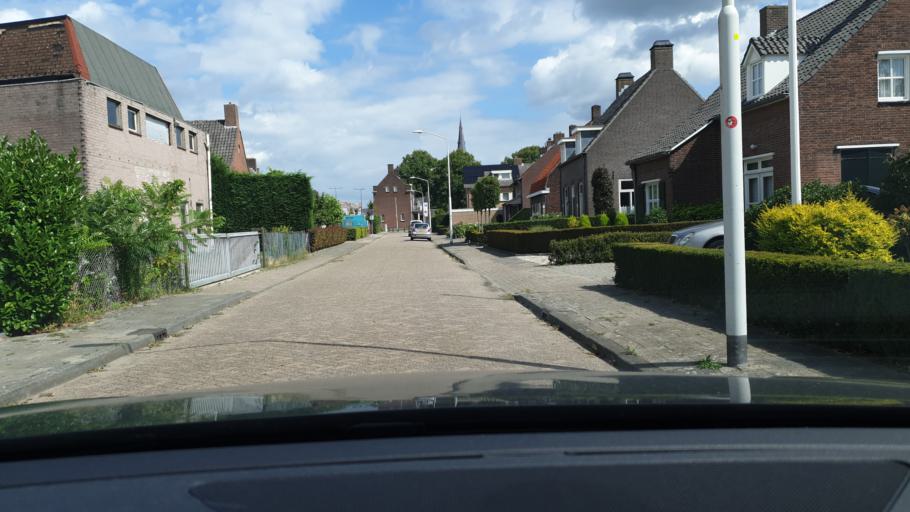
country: NL
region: North Brabant
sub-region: Gemeente Best
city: Best
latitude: 51.5096
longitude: 5.3862
